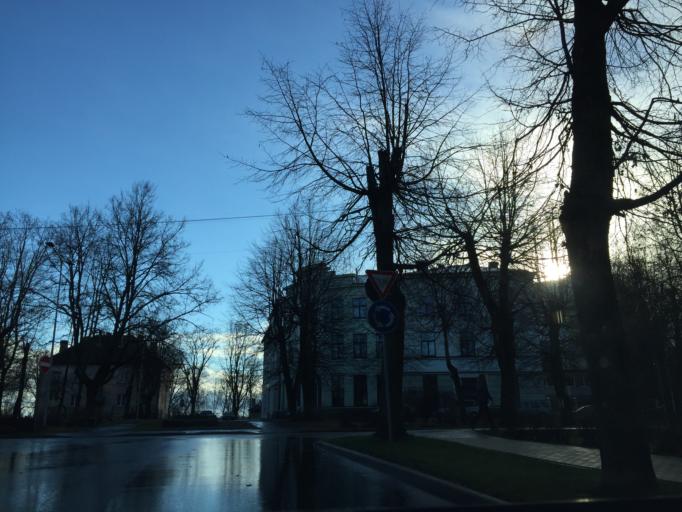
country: LV
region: Valmieras Rajons
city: Valmiera
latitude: 57.5370
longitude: 25.4201
